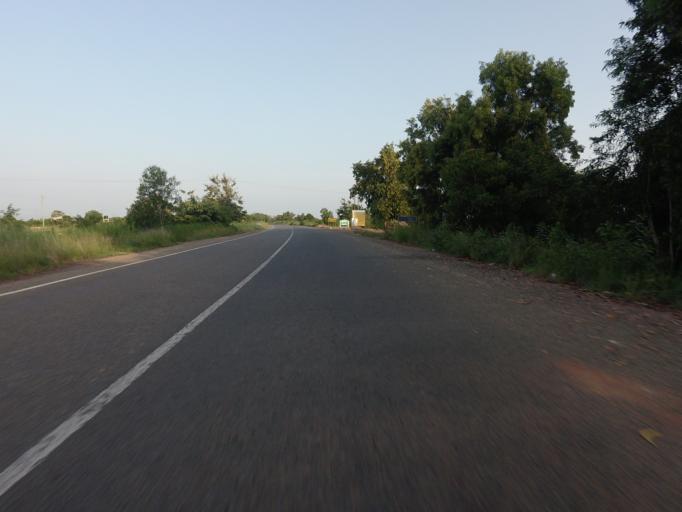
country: GH
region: Volta
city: Anloga
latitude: 5.8964
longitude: 0.7146
